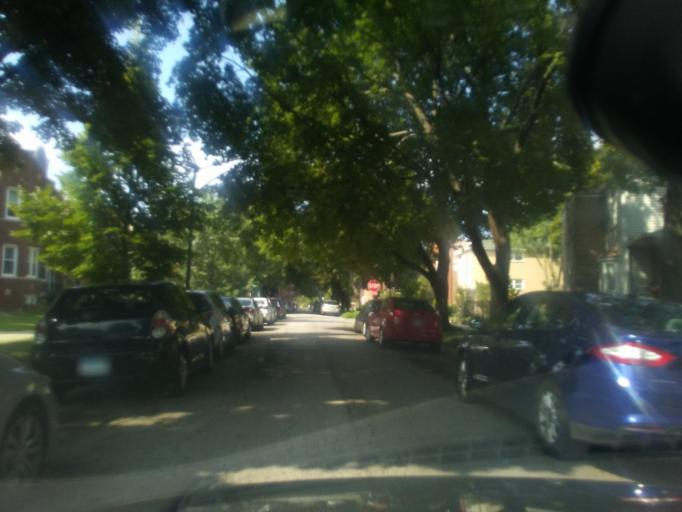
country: US
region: Illinois
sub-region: Cook County
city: Harwood Heights
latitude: 41.9719
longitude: -87.7710
